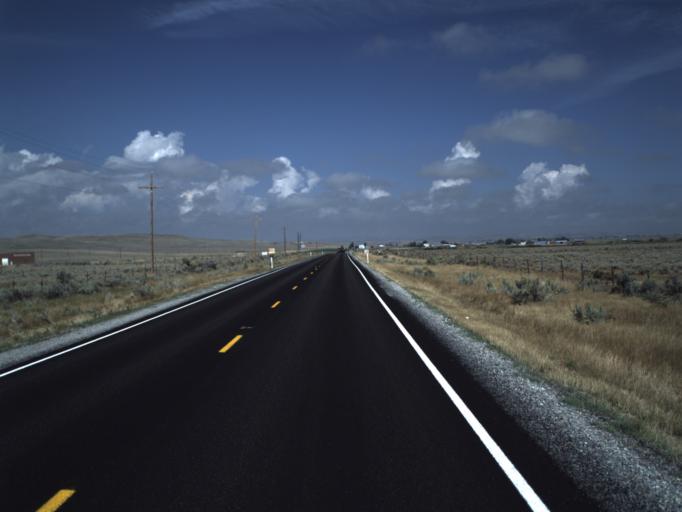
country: US
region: Utah
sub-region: Rich County
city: Randolph
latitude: 41.5840
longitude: -111.1674
